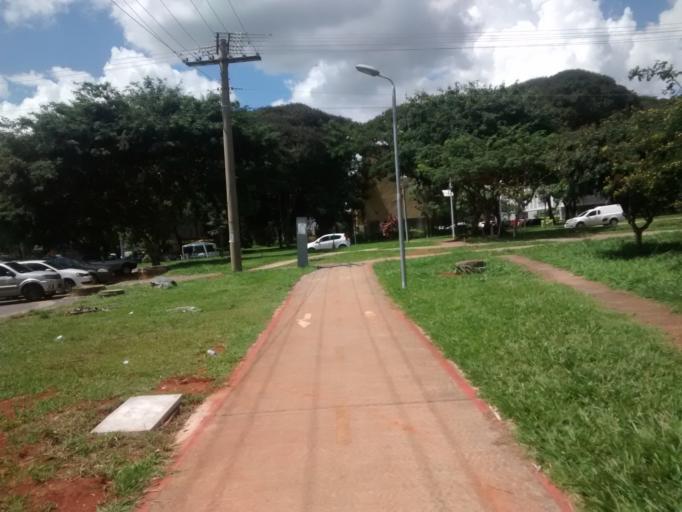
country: BR
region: Federal District
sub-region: Brasilia
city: Brasilia
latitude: -15.7515
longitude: -47.8844
